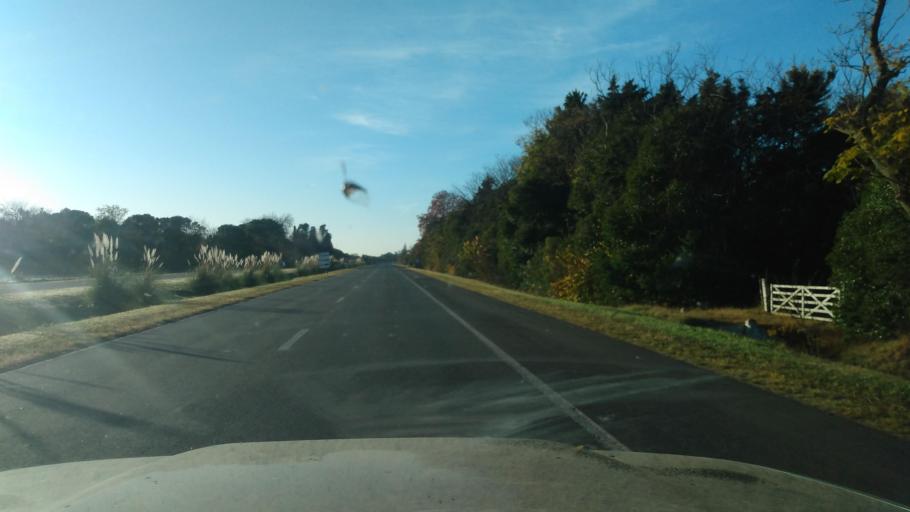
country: AR
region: Buenos Aires
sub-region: Partido de Lujan
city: Lujan
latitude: -34.5461
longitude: -59.2083
